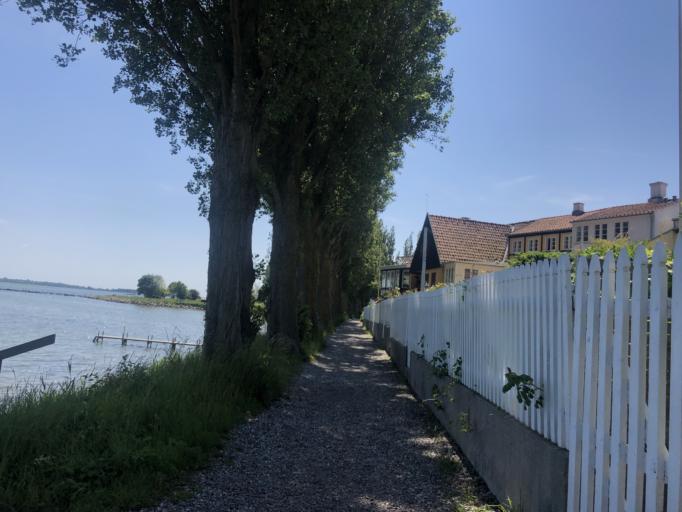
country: DK
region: South Denmark
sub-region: AEro Kommune
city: AEroskobing
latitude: 54.8873
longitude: 10.4143
